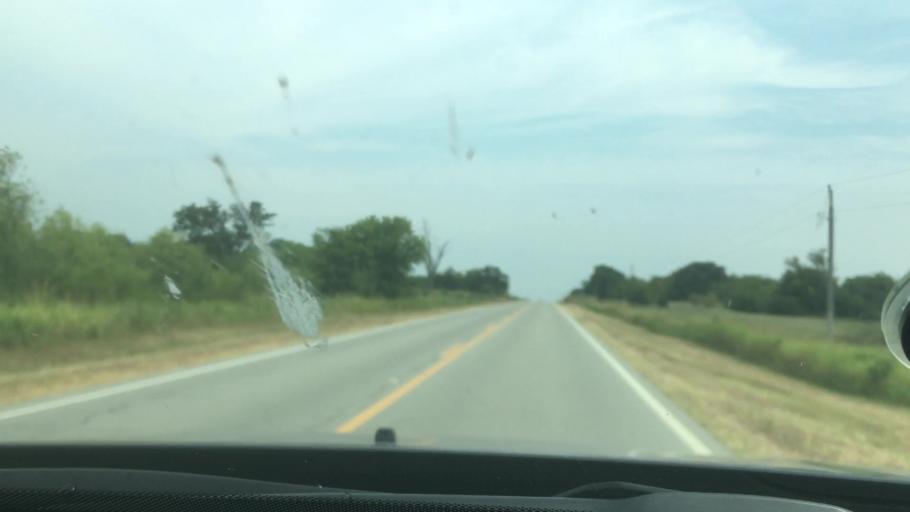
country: US
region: Oklahoma
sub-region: Coal County
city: Coalgate
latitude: 34.5540
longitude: -96.4069
